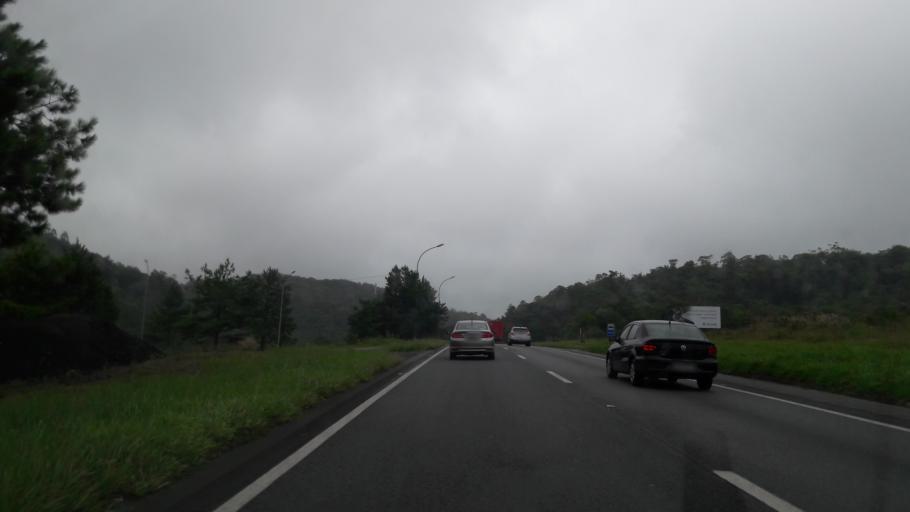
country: BR
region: Parana
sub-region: Campina Grande Do Sul
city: Campina Grande do Sul
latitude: -25.1070
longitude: -48.8055
